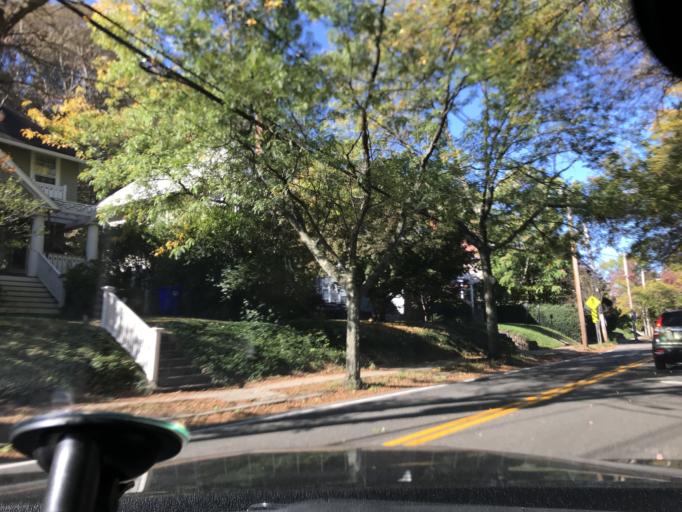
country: US
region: Massachusetts
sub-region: Norfolk County
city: Brookline
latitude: 42.3446
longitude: -71.1303
